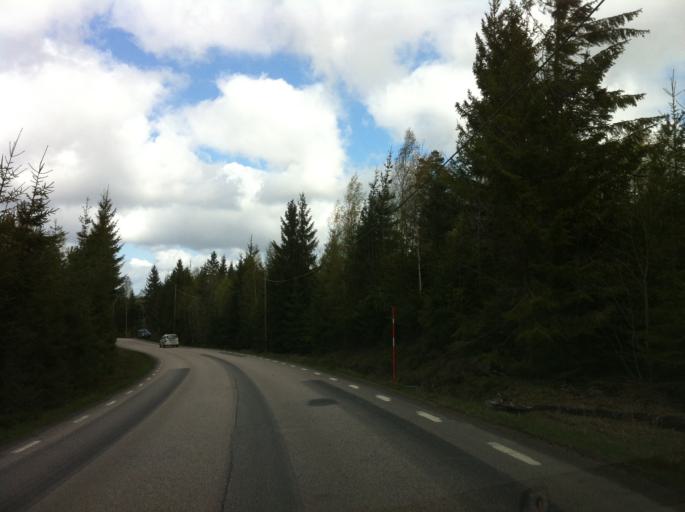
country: SE
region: Vaestra Goetaland
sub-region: Alingsas Kommun
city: Ingared
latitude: 57.8246
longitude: 12.5696
